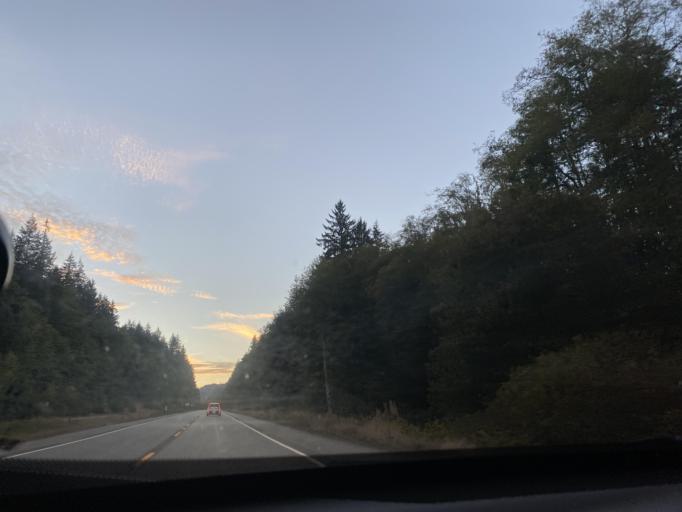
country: US
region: Washington
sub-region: Clallam County
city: Port Angeles
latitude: 48.0696
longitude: -123.6275
